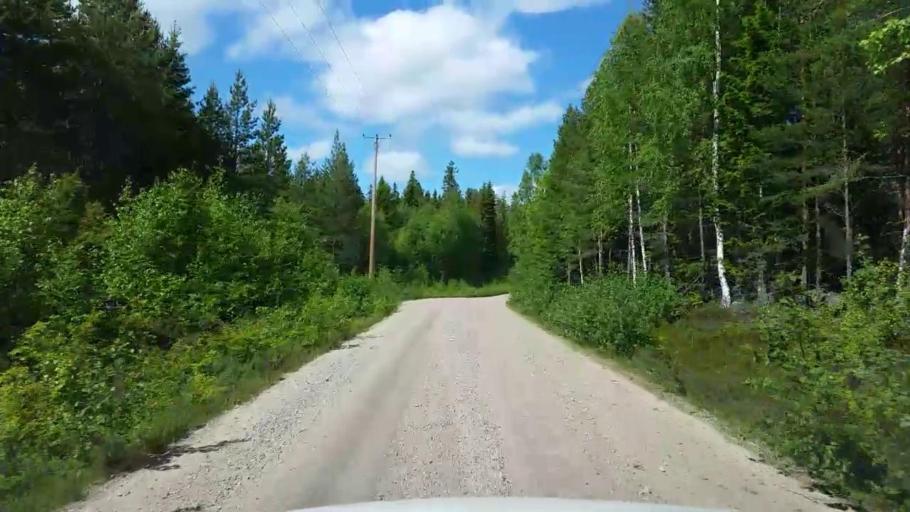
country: SE
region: Gaevleborg
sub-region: Ovanakers Kommun
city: Edsbyn
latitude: 61.5353
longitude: 15.9575
